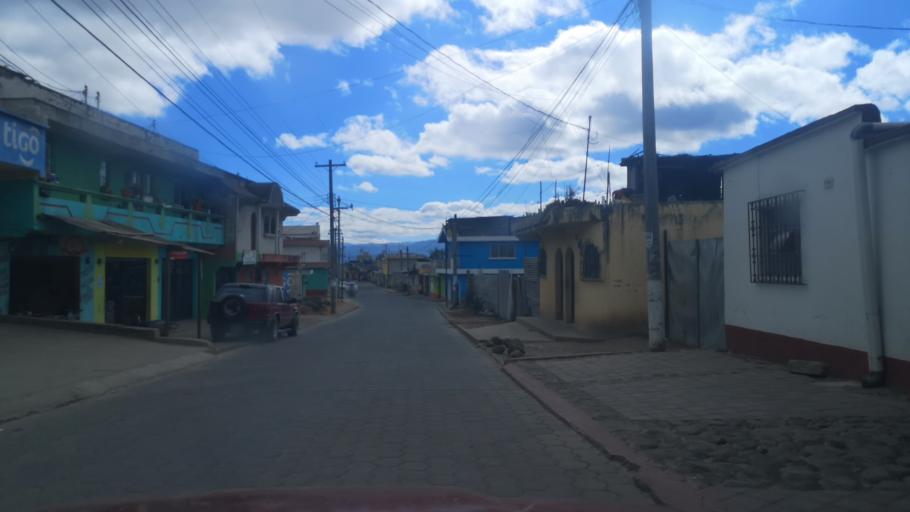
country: GT
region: Quetzaltenango
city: Quetzaltenango
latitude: 14.8367
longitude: -91.5402
